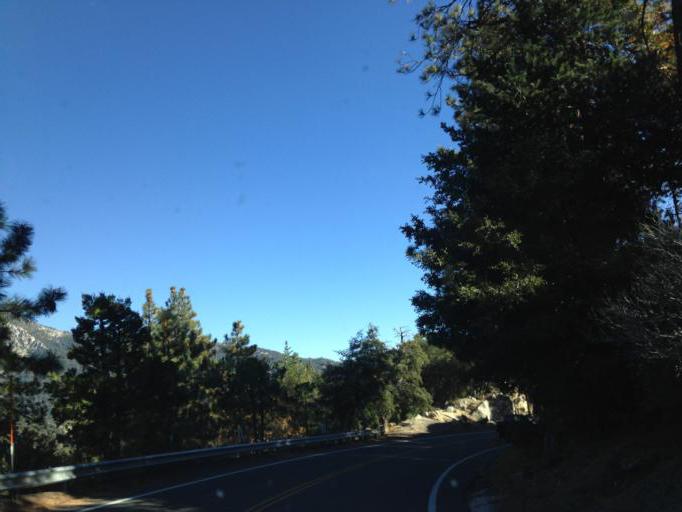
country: US
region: California
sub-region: Riverside County
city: Idyllwild-Pine Cove
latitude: 33.7554
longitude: -116.7357
